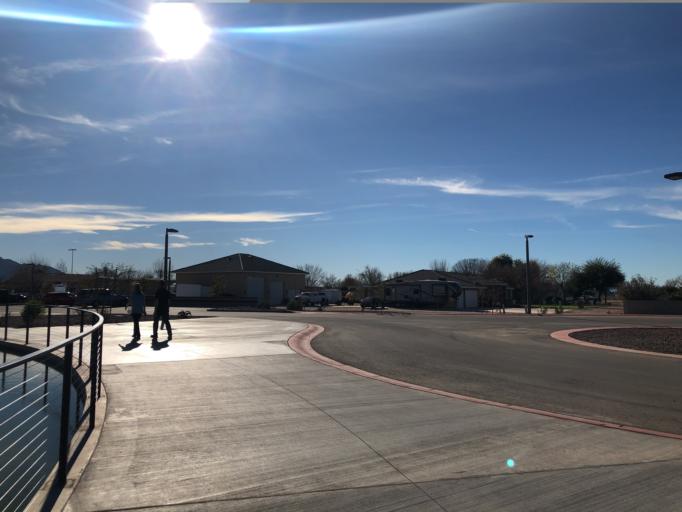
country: US
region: Arizona
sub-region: Maricopa County
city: Queen Creek
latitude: 33.2571
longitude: -111.6600
